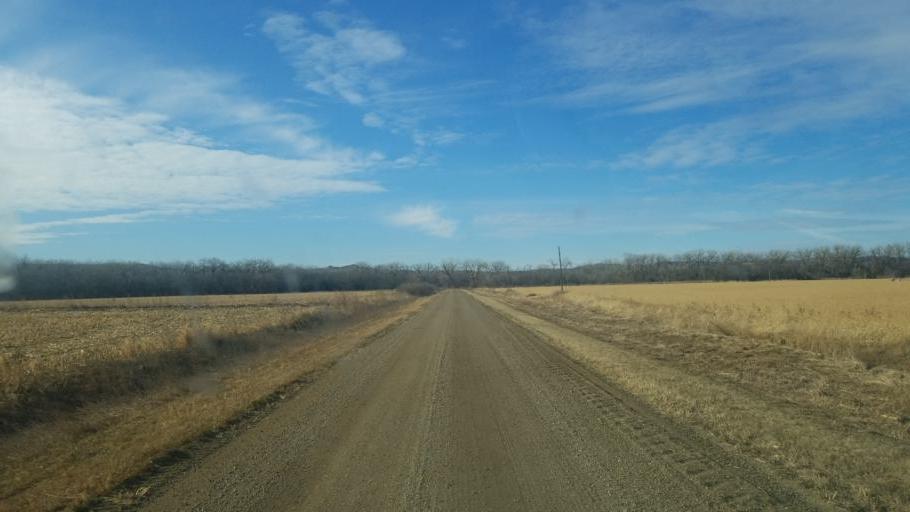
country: US
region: South Dakota
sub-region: Charles Mix County
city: Wagner
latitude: 42.9407
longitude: -98.4403
